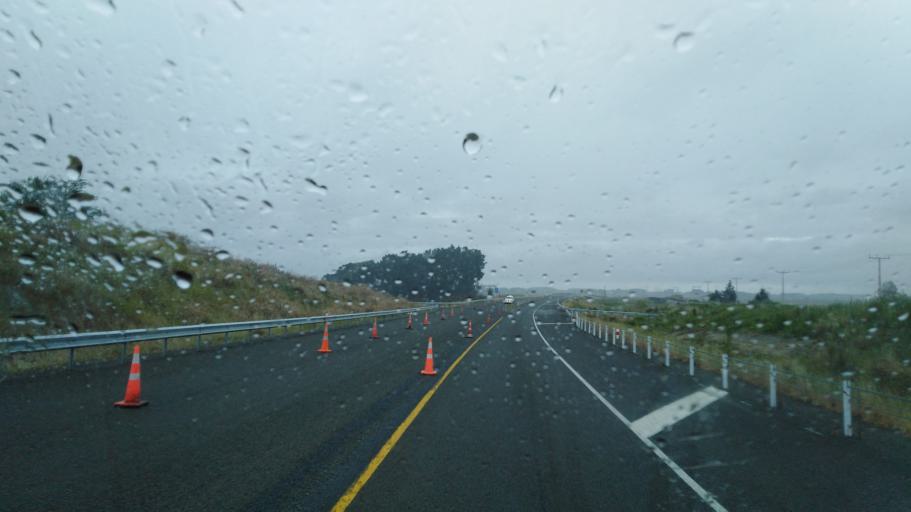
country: NZ
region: Manawatu-Wanganui
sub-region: Horowhenua District
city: Foxton
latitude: -40.5188
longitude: 175.2758
